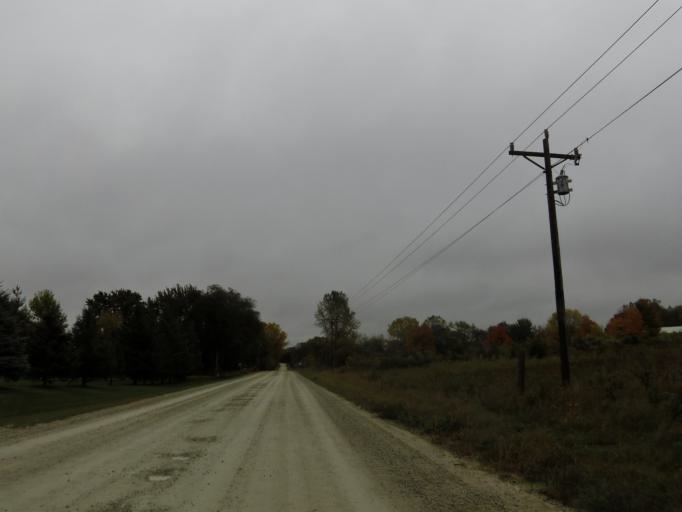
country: US
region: Minnesota
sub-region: Scott County
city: Prior Lake
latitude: 44.6886
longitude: -93.4477
